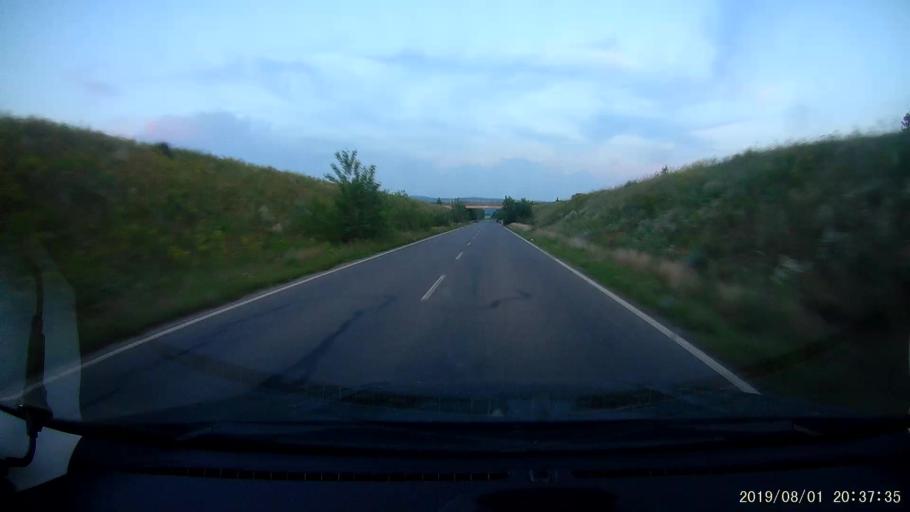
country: BG
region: Yambol
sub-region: Obshtina Elkhovo
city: Elkhovo
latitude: 42.0449
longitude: 26.5949
